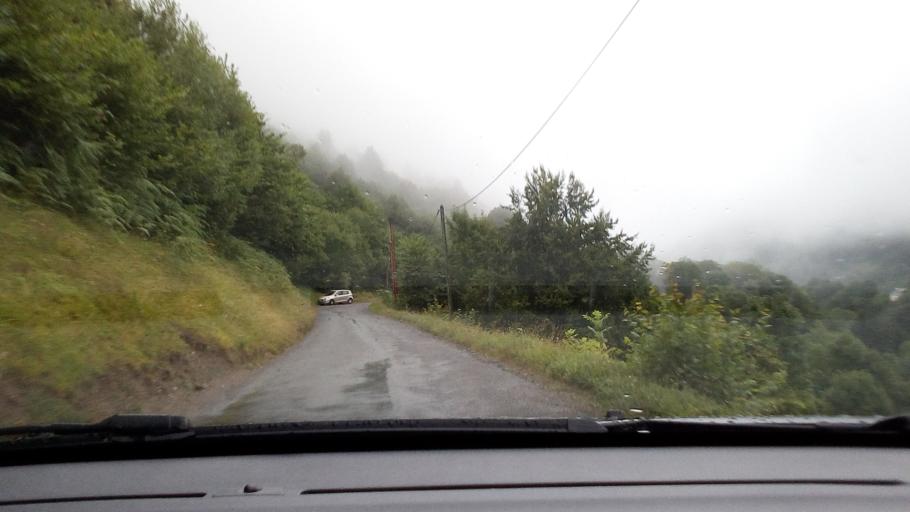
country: FR
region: Midi-Pyrenees
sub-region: Departement des Hautes-Pyrenees
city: Cauterets
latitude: 42.9447
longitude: -0.2277
